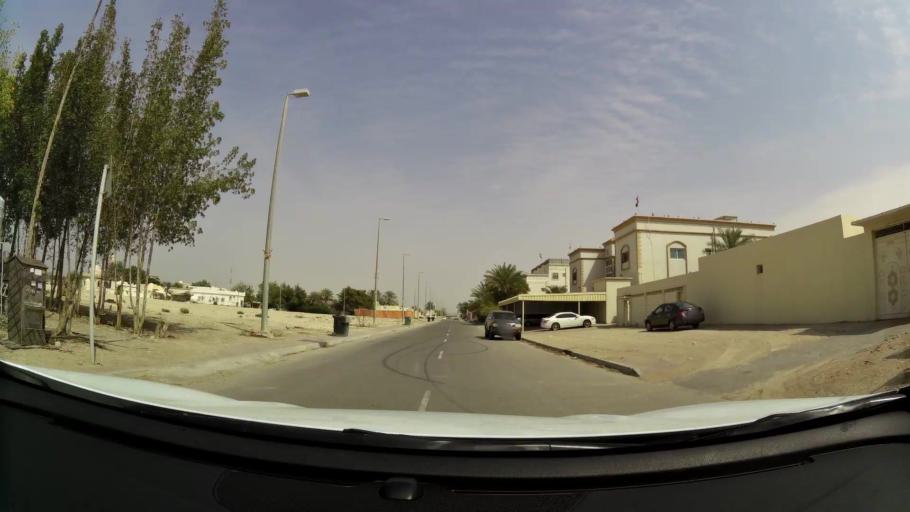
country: AE
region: Abu Dhabi
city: Abu Dhabi
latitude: 24.5428
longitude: 54.6799
